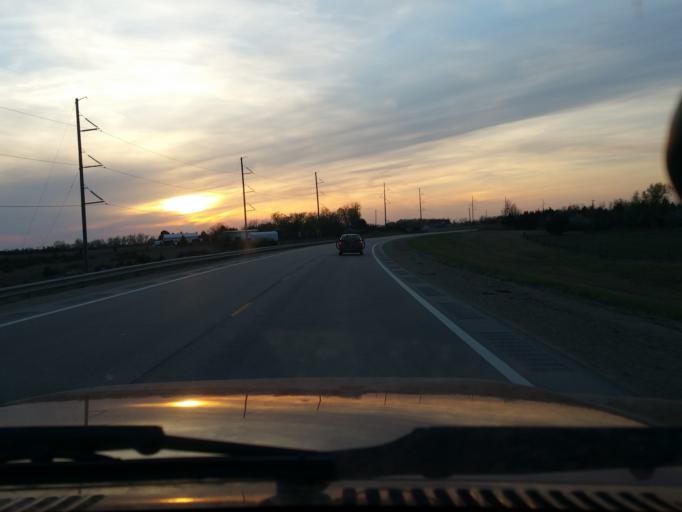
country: US
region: Kansas
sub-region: Riley County
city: Manhattan
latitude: 39.2525
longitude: -96.6687
